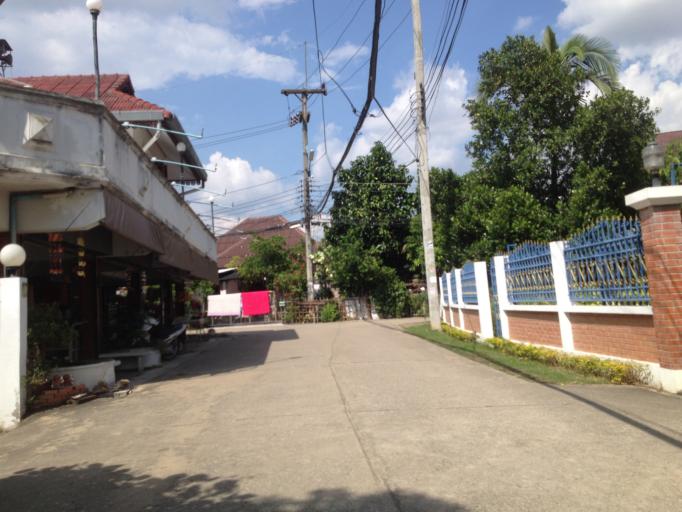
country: TH
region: Chiang Mai
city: Hang Dong
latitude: 18.7364
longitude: 98.9290
